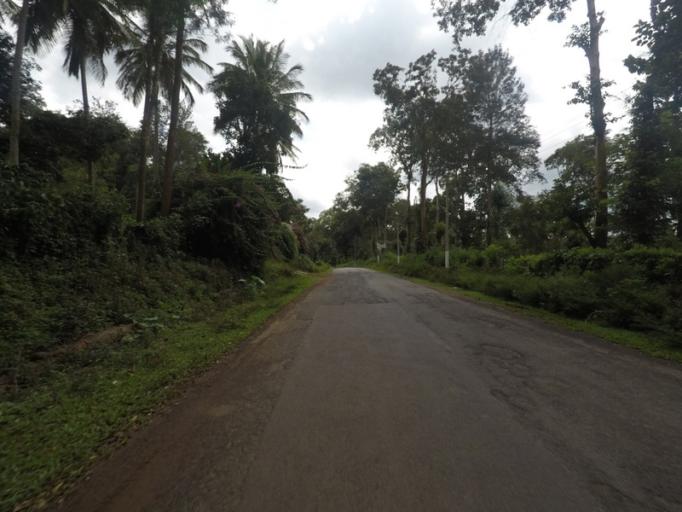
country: IN
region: Karnataka
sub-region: Kodagu
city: Suntikoppa
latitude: 12.3631
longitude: 75.8860
